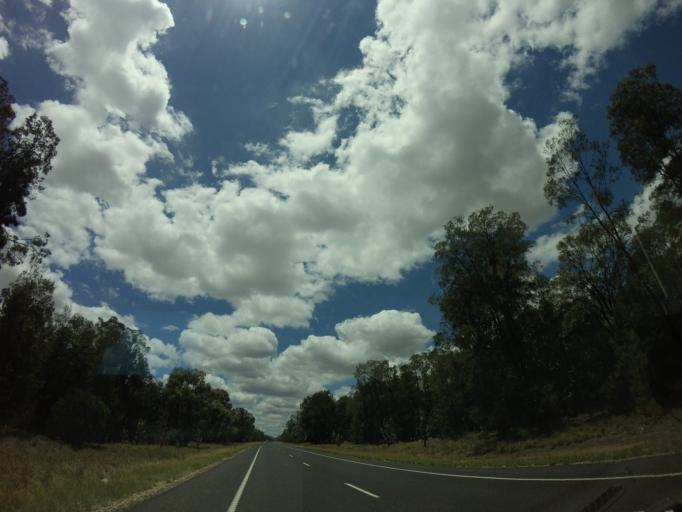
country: AU
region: Queensland
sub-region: Goondiwindi
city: Goondiwindi
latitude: -28.0879
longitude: 150.7322
